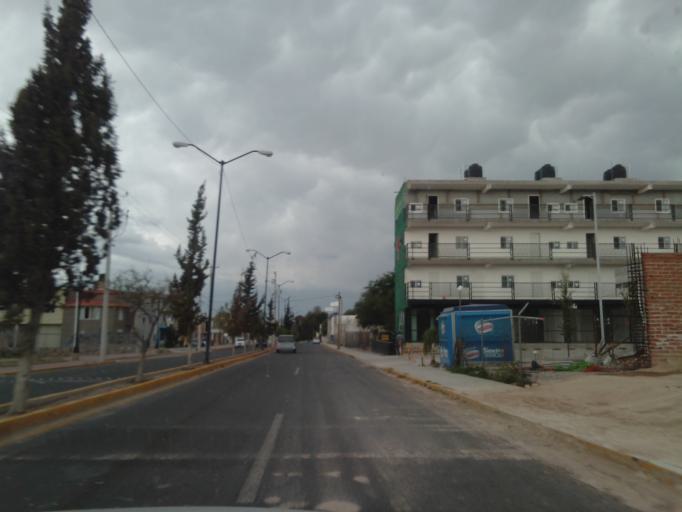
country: MX
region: Guanajuato
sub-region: Dolores Hidalgo Cuna de la Independencia Nacional
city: Colonia Padre Hidalgo
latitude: 21.1667
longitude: -100.9329
